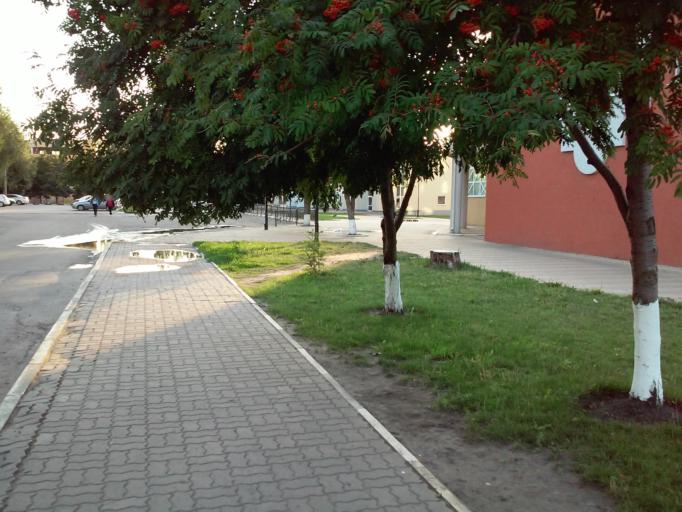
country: RU
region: Belgorod
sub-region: Belgorodskiy Rayon
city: Belgorod
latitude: 50.5745
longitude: 36.5786
